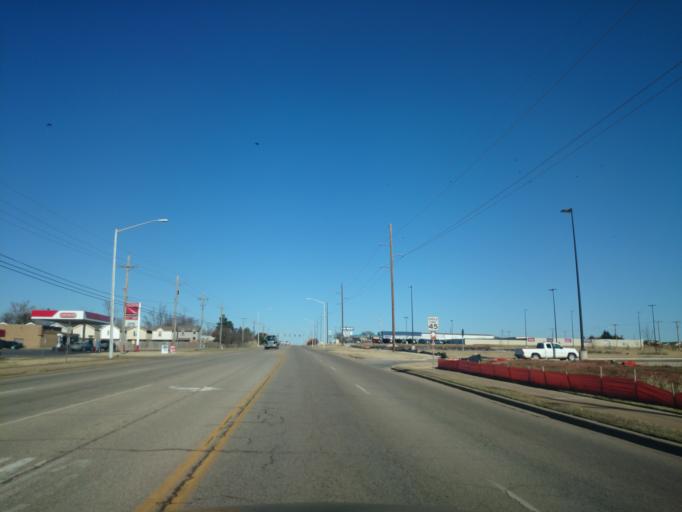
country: US
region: Oklahoma
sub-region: Payne County
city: Stillwater
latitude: 36.1453
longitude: -97.0516
